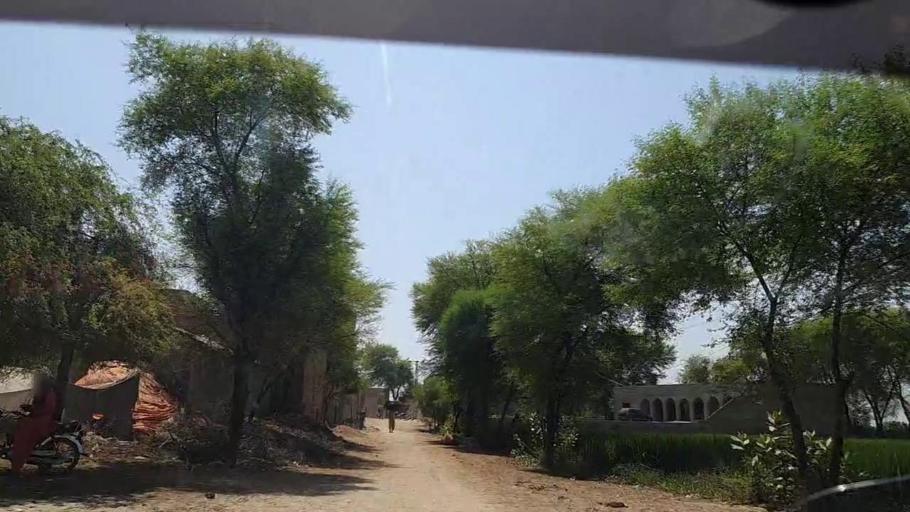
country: PK
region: Sindh
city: Ghauspur
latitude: 28.1655
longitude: 69.1257
